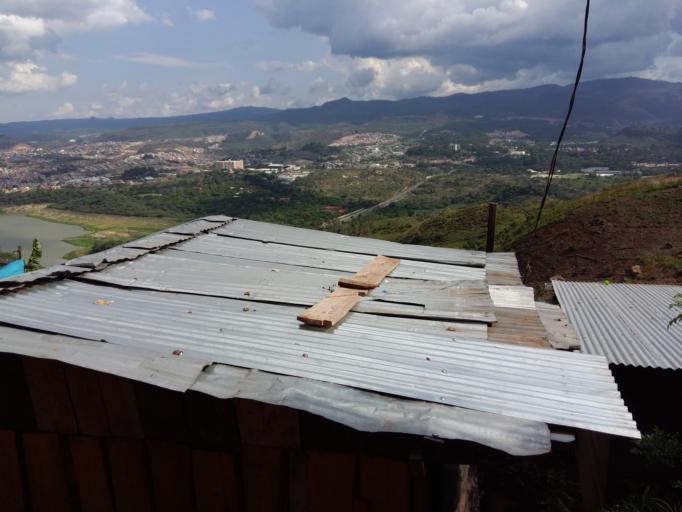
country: HN
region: Francisco Morazan
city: Tegucigalpa
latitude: 14.0764
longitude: -87.2498
